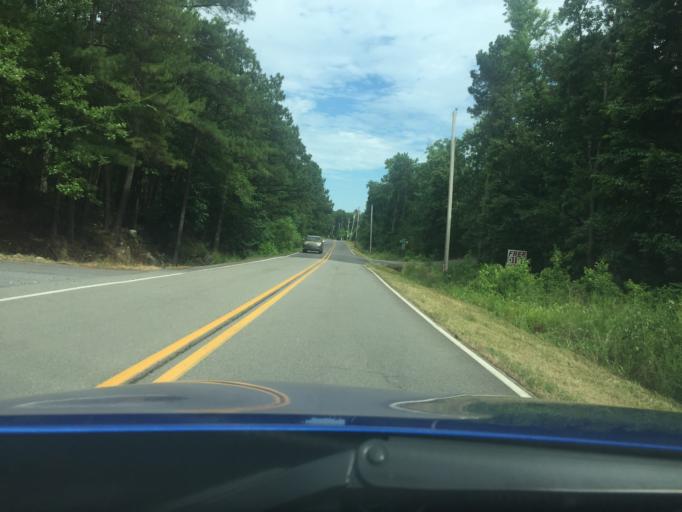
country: US
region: Arkansas
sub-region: Pulaski County
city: Maumelle
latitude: 34.8341
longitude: -92.4541
